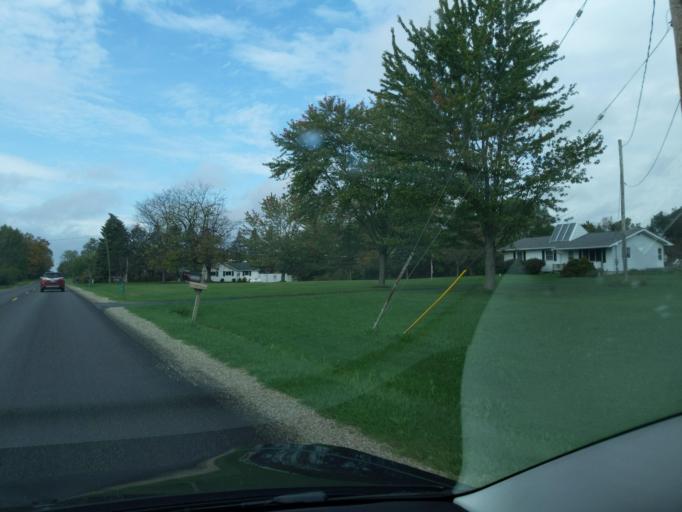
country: US
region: Michigan
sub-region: Eaton County
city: Dimondale
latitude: 42.6257
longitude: -84.6457
